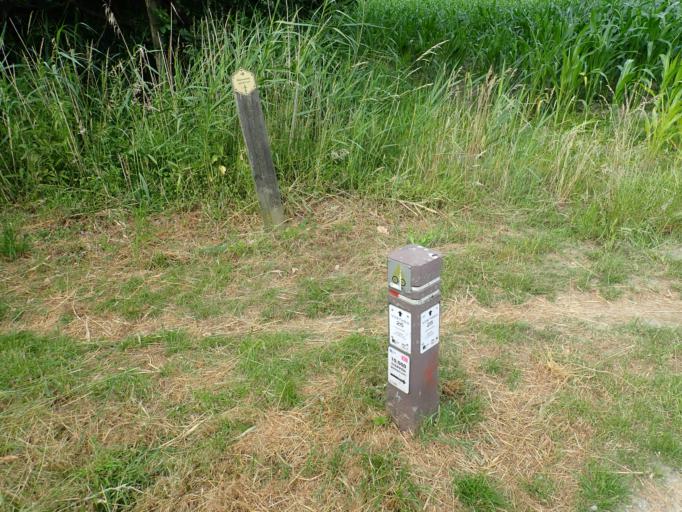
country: BE
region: Flanders
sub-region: Provincie Oost-Vlaanderen
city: Hamme
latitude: 51.1120
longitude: 4.1671
